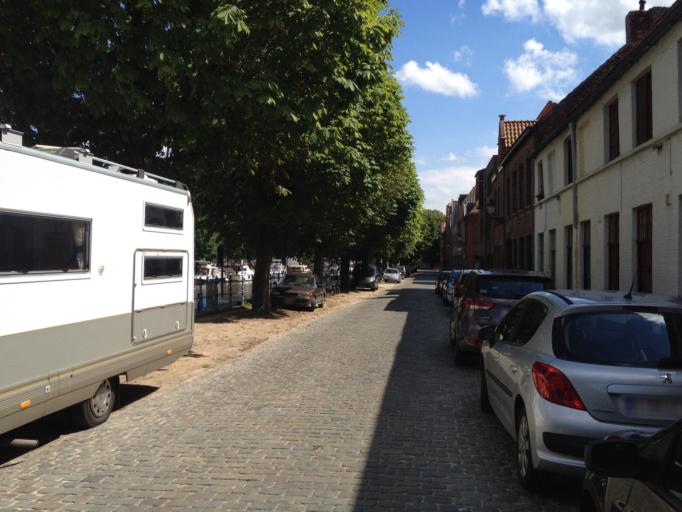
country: BE
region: Flanders
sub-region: Provincie West-Vlaanderen
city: Brugge
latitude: 51.2062
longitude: 3.2351
